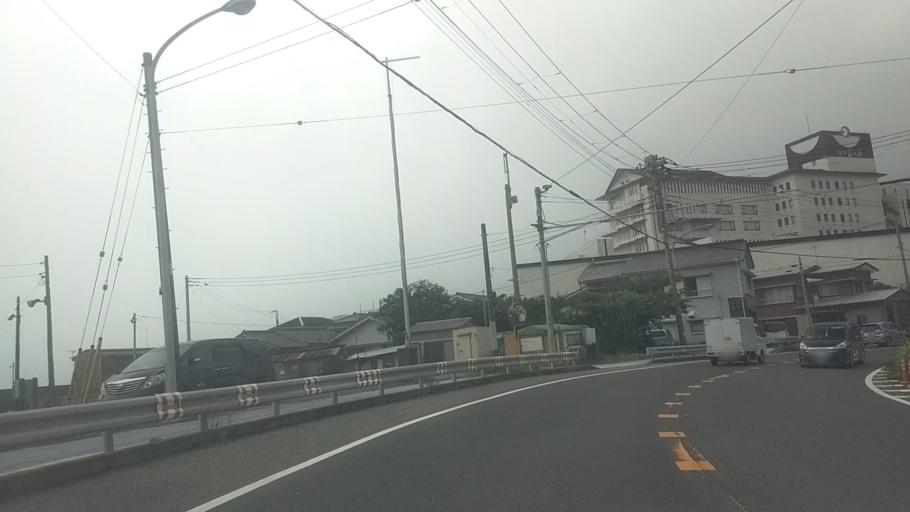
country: JP
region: Chiba
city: Kawaguchi
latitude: 35.1231
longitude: 140.1964
